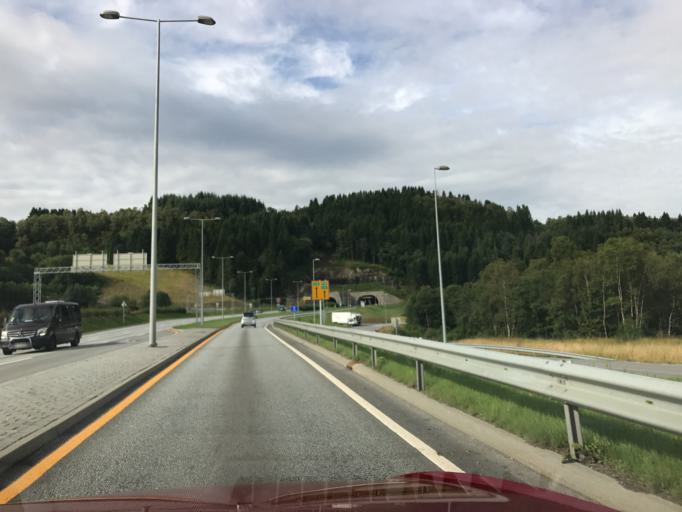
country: NO
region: Hordaland
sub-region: Bergen
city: Hylkje
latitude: 60.4818
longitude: 5.3713
